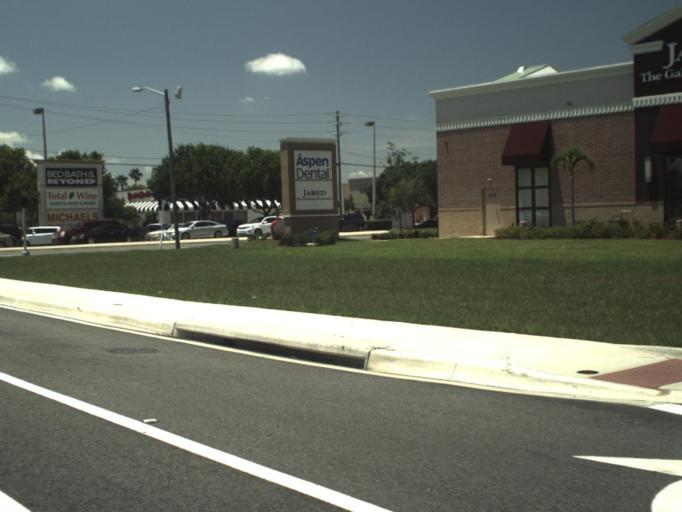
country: US
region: Florida
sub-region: Martin County
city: North River Shores
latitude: 27.2375
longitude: -80.2694
